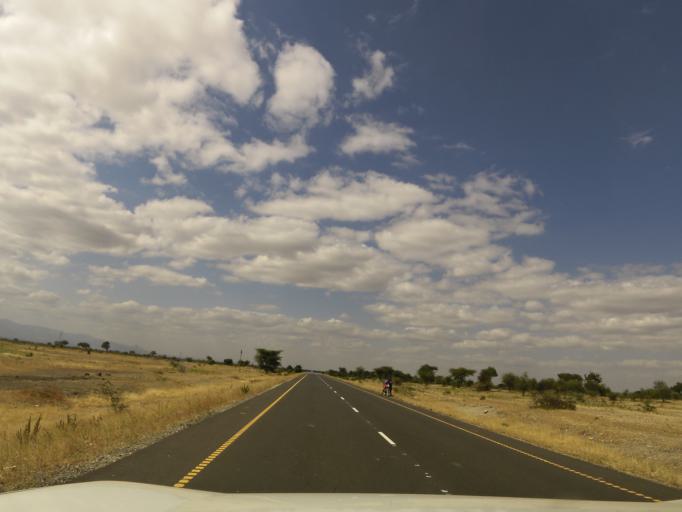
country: TZ
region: Arusha
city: Mto wa Mbu
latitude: -3.6571
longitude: 35.9771
